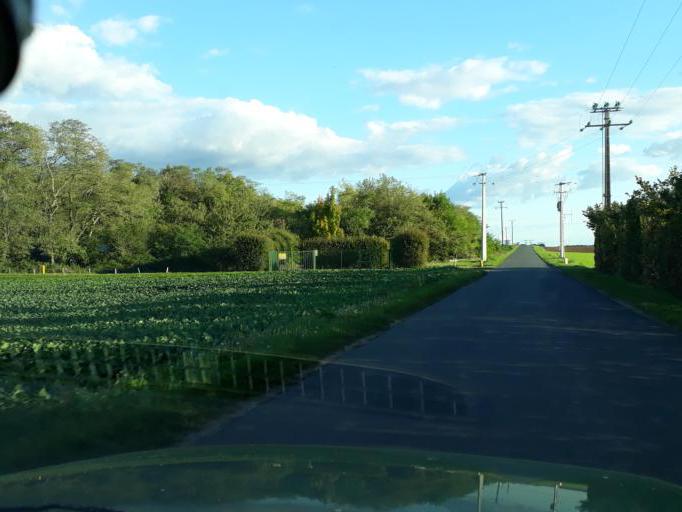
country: FR
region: Centre
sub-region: Departement du Loir-et-Cher
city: Mer
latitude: 47.7876
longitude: 1.5303
